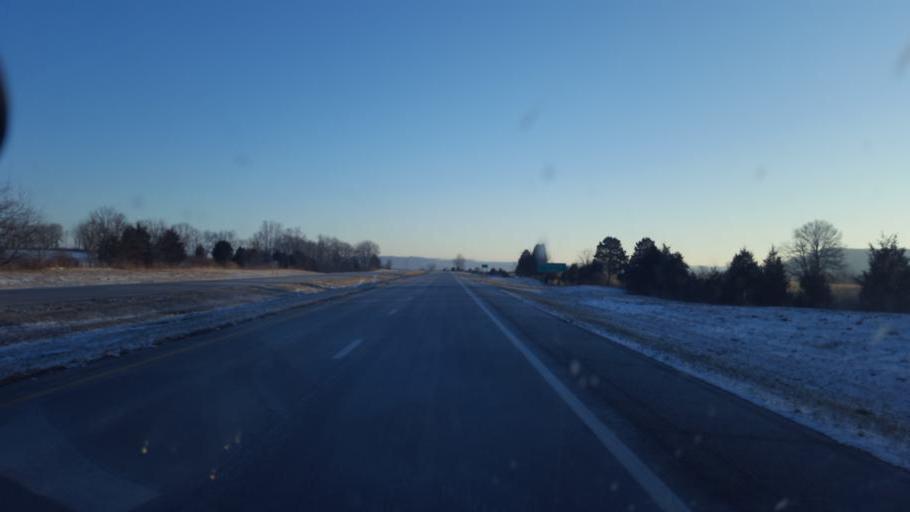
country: US
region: Ohio
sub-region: Adams County
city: Peebles
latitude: 38.9512
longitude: -83.3730
